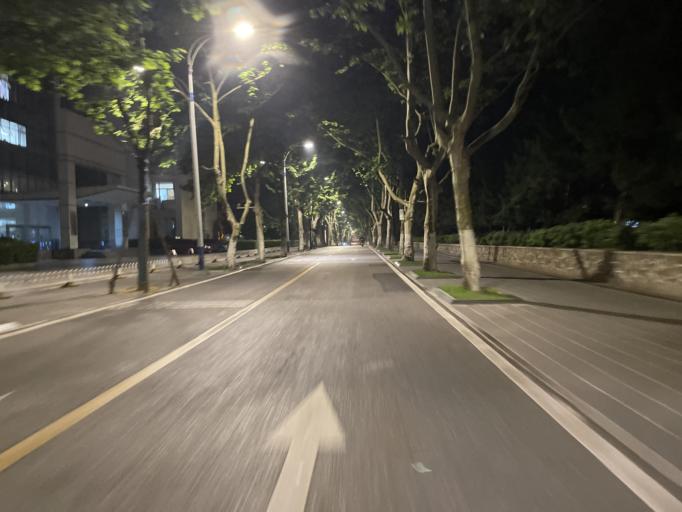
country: CN
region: Hubei
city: Guanshan
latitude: 30.5156
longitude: 114.4071
